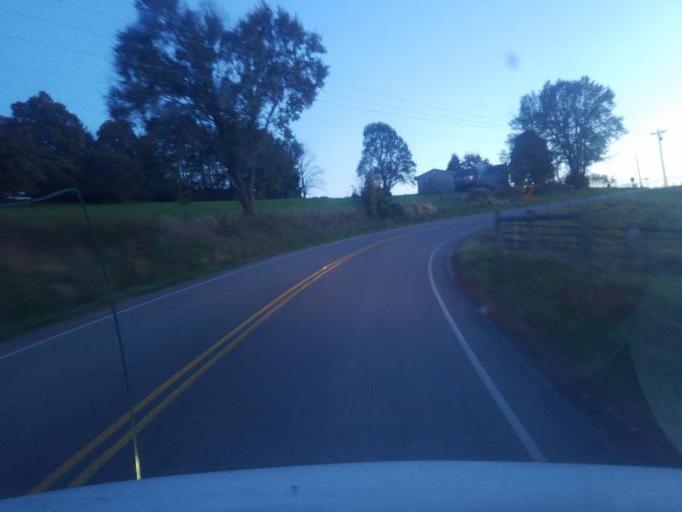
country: US
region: Ohio
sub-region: Perry County
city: Somerset
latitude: 39.8621
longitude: -82.2484
